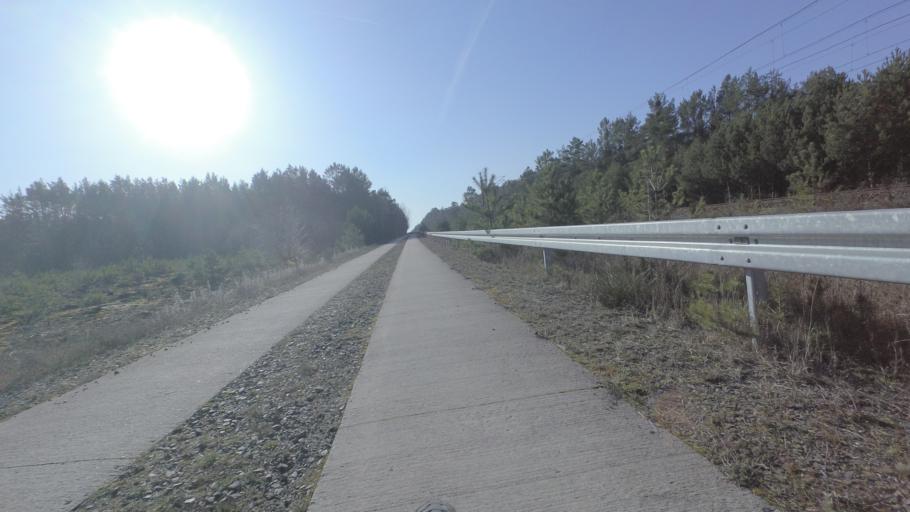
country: DE
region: Brandenburg
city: Trebbin
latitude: 52.1631
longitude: 13.2210
